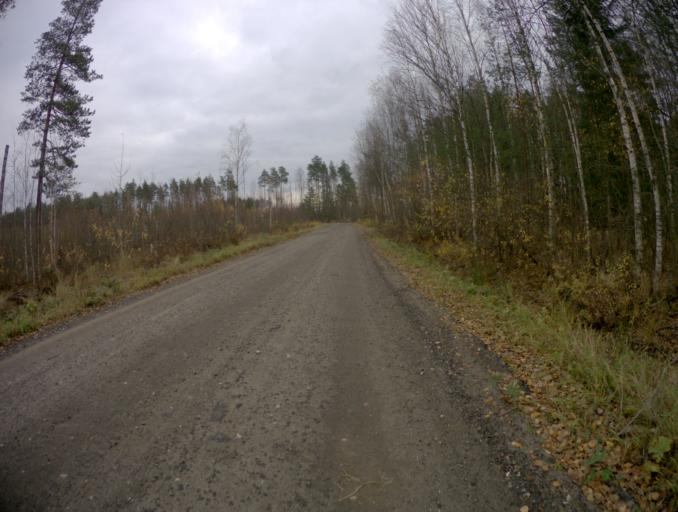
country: RU
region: Moskovskaya
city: Malaya Dubna
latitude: 55.9253
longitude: 38.9911
